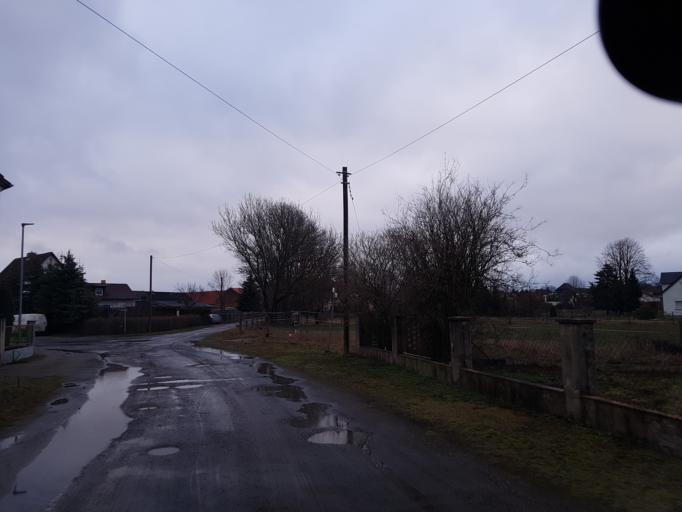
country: DE
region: Brandenburg
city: Plessa
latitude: 51.4619
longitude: 13.6160
